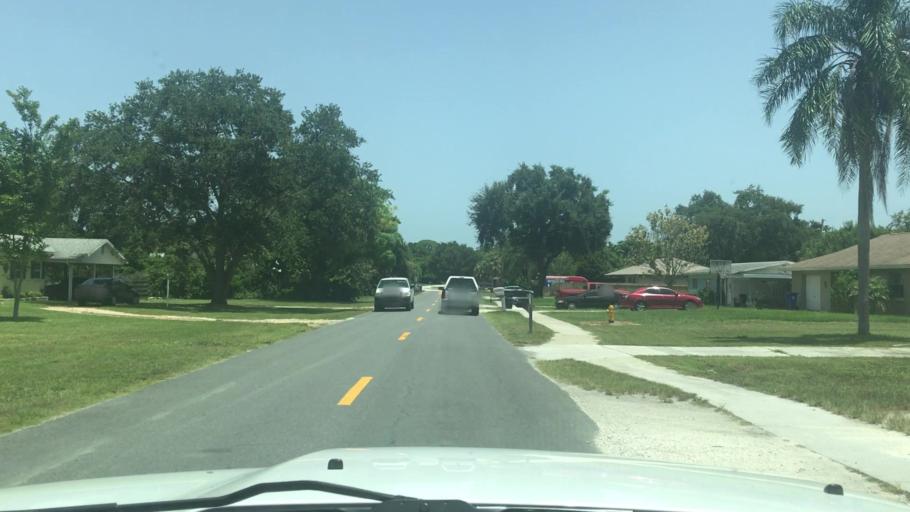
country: US
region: Florida
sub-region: Indian River County
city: Vero Beach
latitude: 27.6434
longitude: -80.4156
